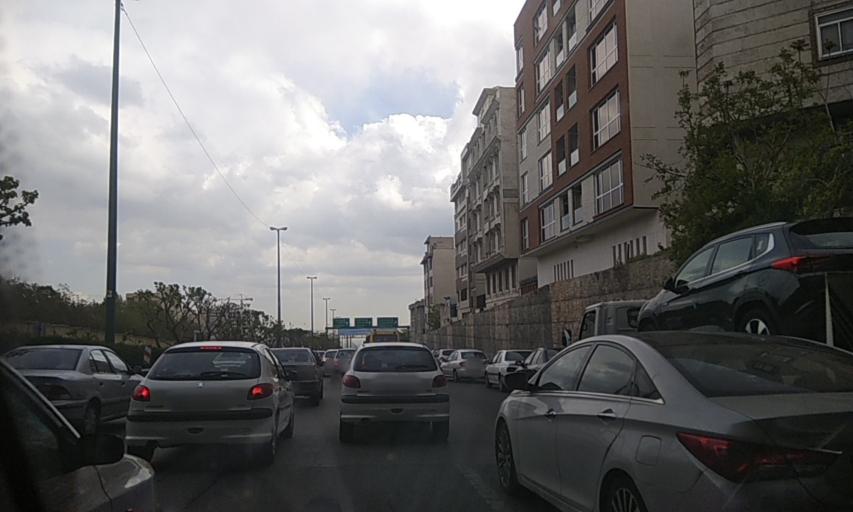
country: IR
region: Tehran
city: Tajrish
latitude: 35.7754
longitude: 51.3442
